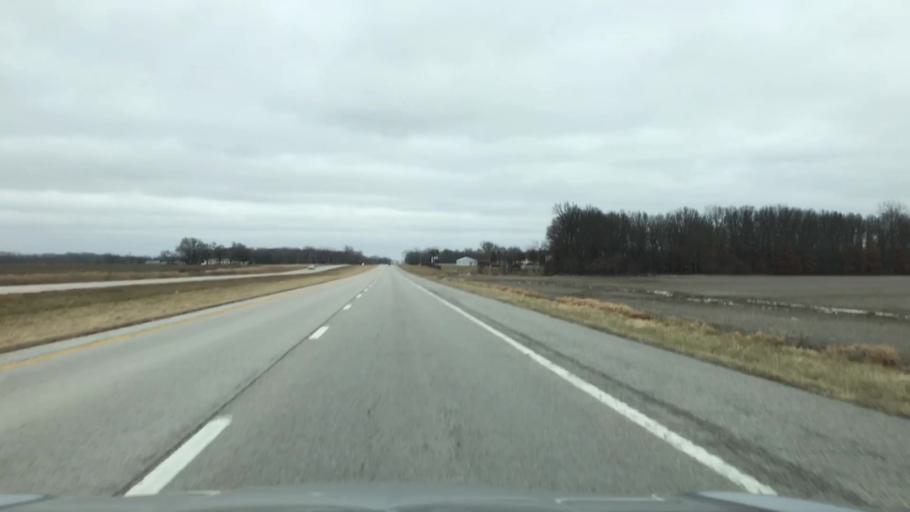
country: US
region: Missouri
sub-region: Livingston County
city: Chillicothe
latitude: 39.7765
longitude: -93.4510
